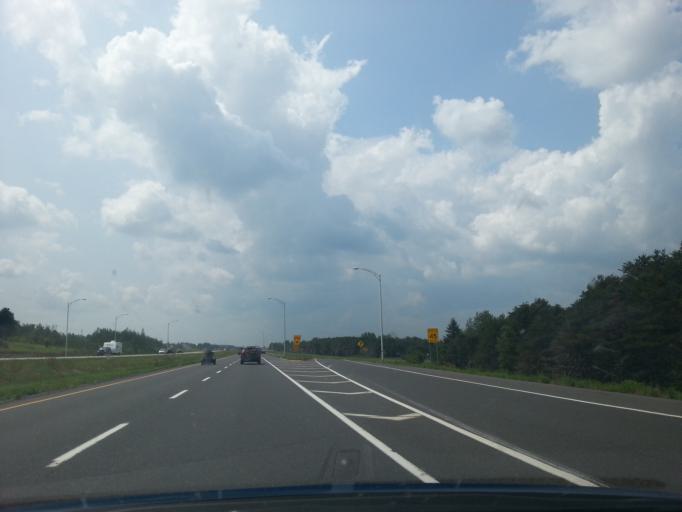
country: CA
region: Quebec
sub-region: Capitale-Nationale
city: Saint-Augustin-de-Desmaures
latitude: 46.6430
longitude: -71.4439
